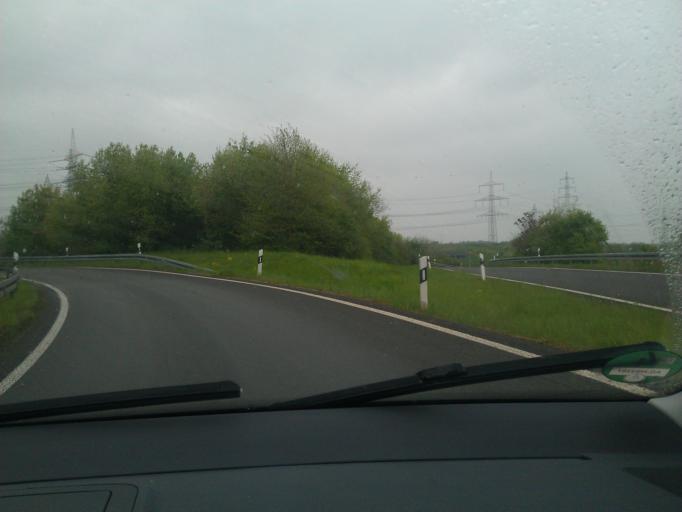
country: DE
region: North Rhine-Westphalia
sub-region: Regierungsbezirk Koln
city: Stossdorf
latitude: 50.7767
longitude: 7.2387
